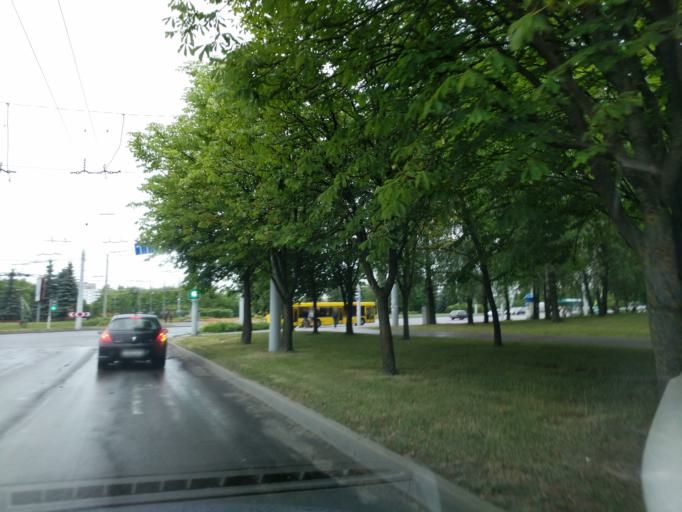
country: BY
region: Minsk
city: Novoye Medvezhino
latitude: 53.8585
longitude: 27.4749
